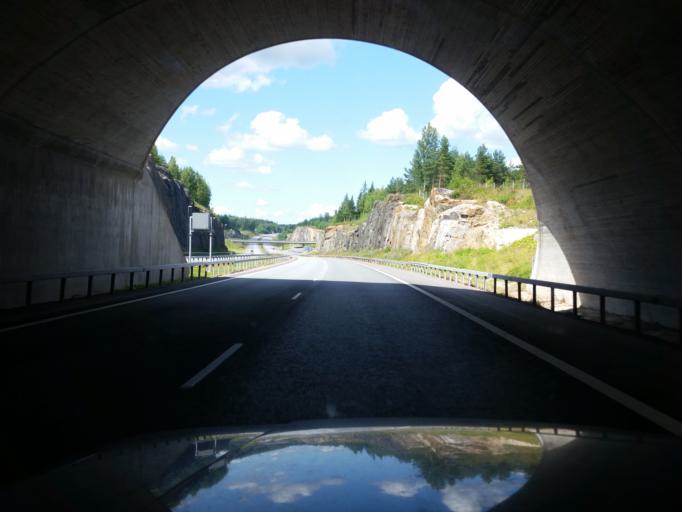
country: FI
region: Uusimaa
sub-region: Helsinki
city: Sammatti
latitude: 60.3769
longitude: 23.8193
